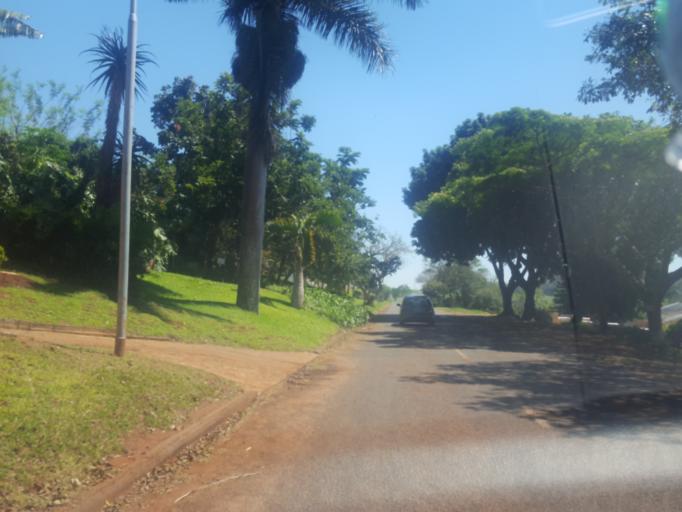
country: ZA
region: KwaZulu-Natal
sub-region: uThungulu District Municipality
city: Empangeni
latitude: -28.7469
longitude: 31.9088
